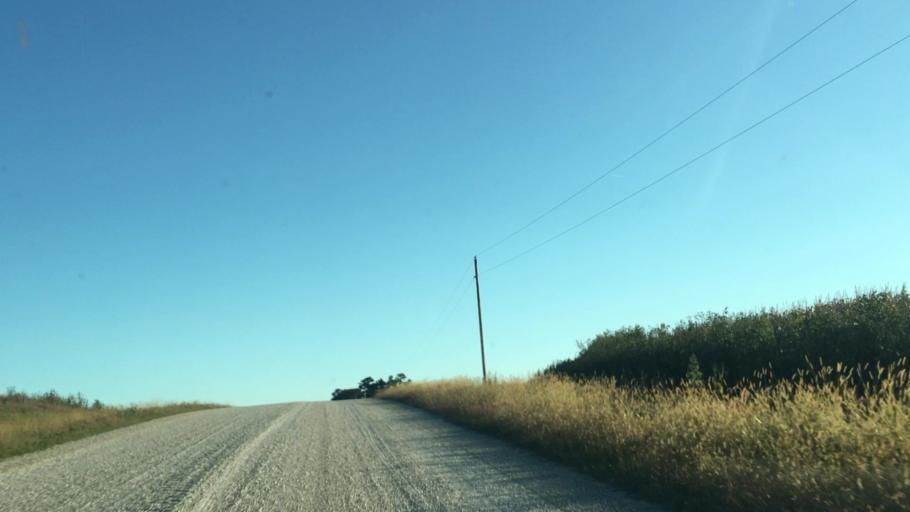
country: US
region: Minnesota
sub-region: Fillmore County
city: Preston
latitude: 43.8124
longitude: -92.0396
